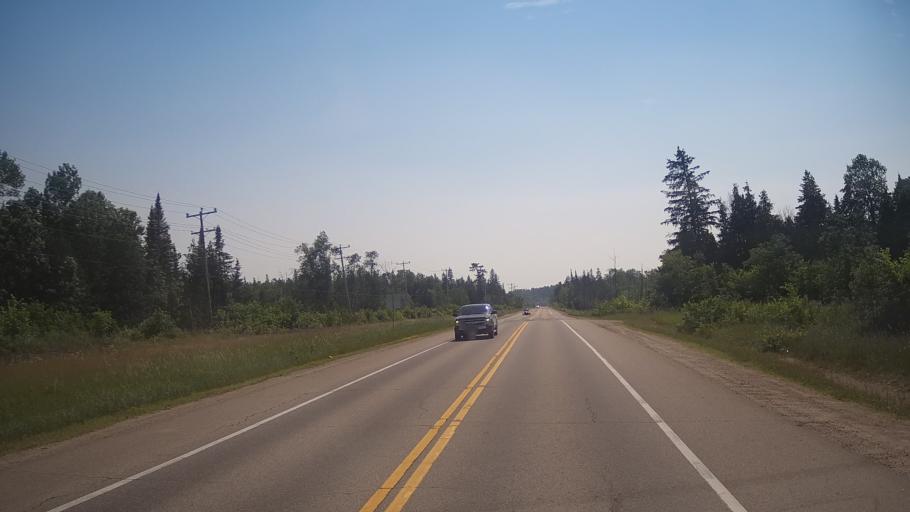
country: CA
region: Ontario
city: Pembroke
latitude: 45.8233
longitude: -77.0191
